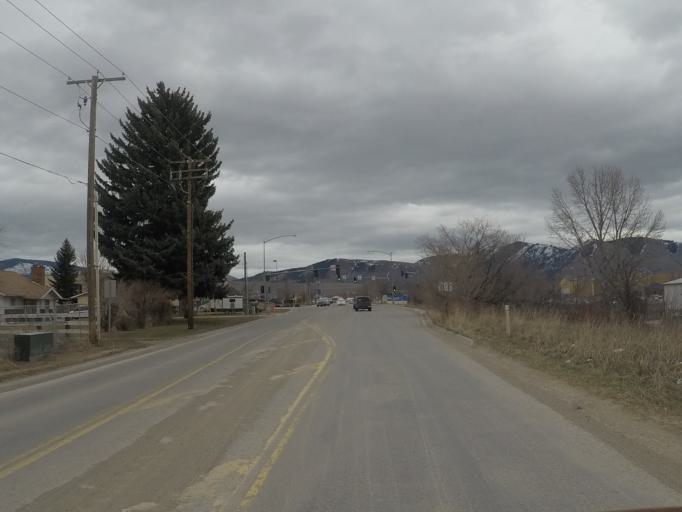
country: US
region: Montana
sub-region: Missoula County
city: Orchard Homes
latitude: 46.8857
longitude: -114.0456
